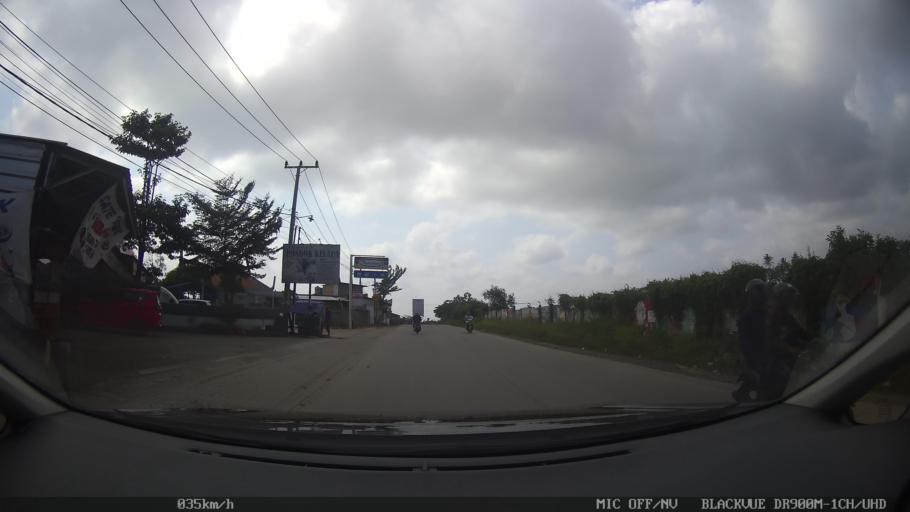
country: ID
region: Lampung
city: Kedaton
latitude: -5.3308
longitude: 105.2918
